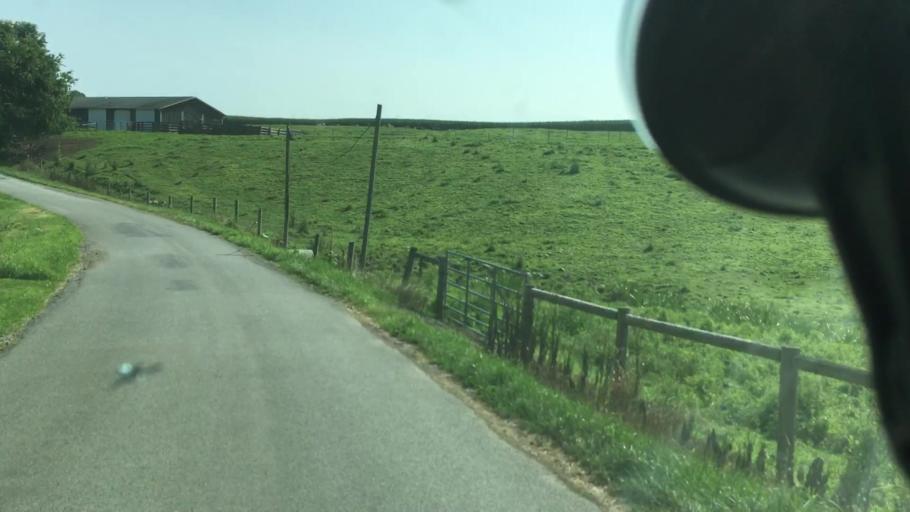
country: US
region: Pennsylvania
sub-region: Butler County
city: Slippery Rock
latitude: 41.0455
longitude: -80.1772
